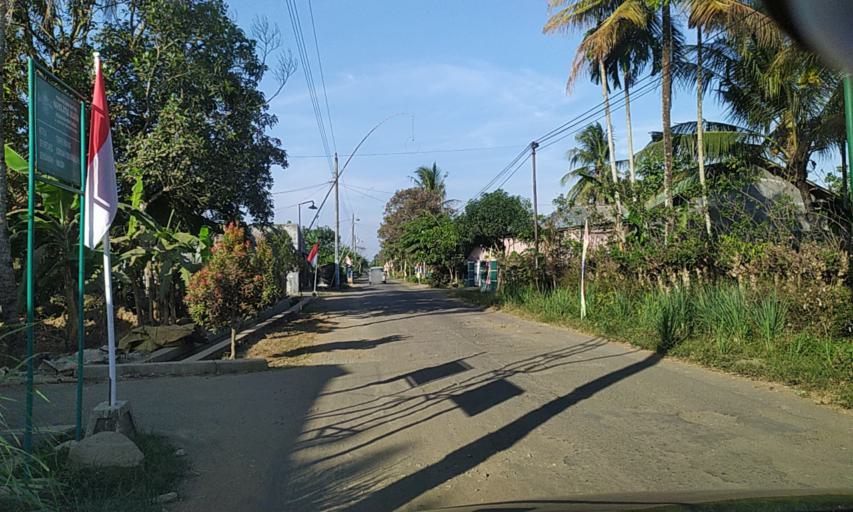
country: ID
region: Central Java
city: Rejanegara
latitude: -7.6686
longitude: 109.0608
